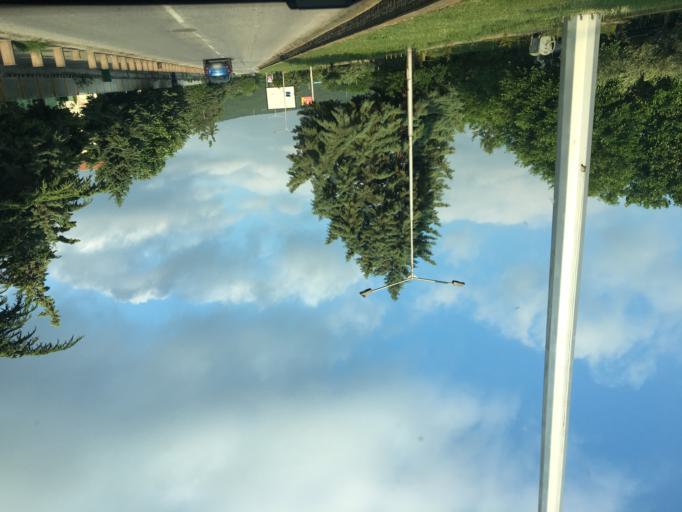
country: MK
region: Valandovo
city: Valandovo
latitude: 41.3155
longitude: 22.5603
